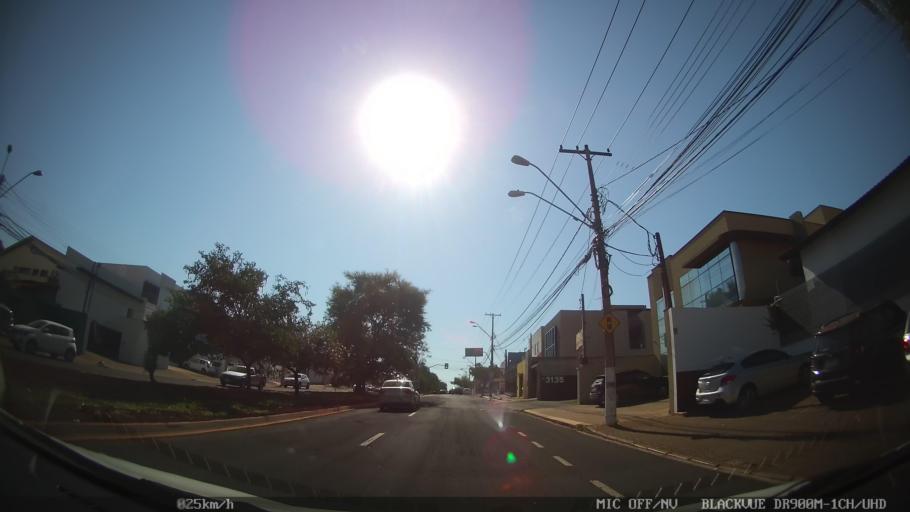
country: BR
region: Sao Paulo
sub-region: Ribeirao Preto
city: Ribeirao Preto
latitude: -21.2021
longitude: -47.8186
